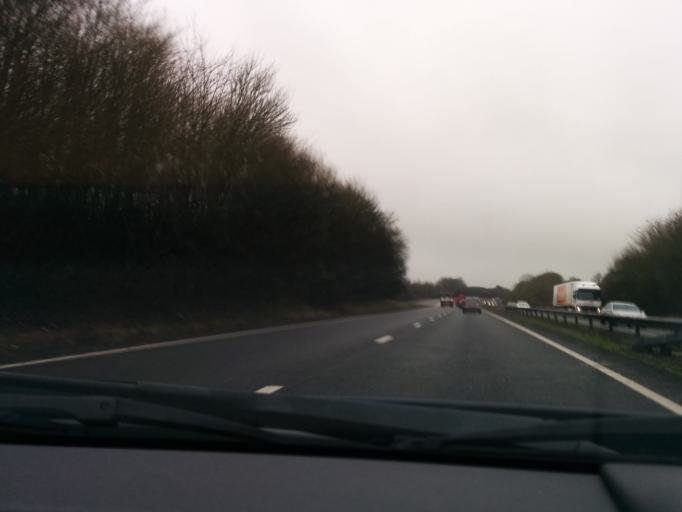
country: GB
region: England
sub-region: Hampshire
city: Highclere
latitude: 51.3173
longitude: -1.3372
